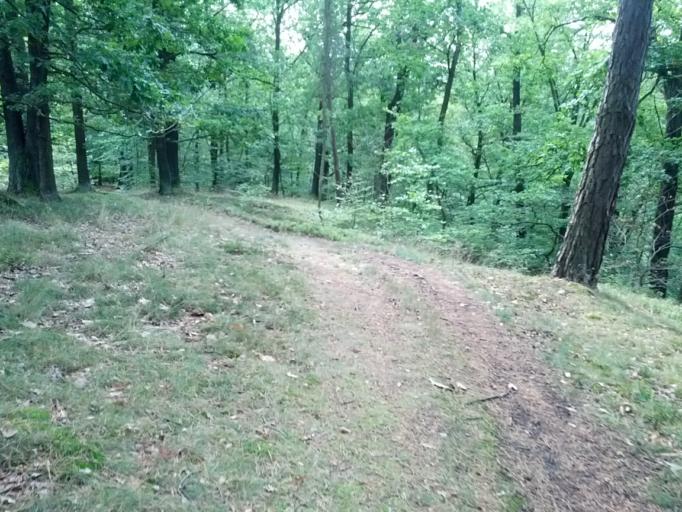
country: DE
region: Thuringia
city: Eisenach
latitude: 50.9559
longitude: 10.3120
